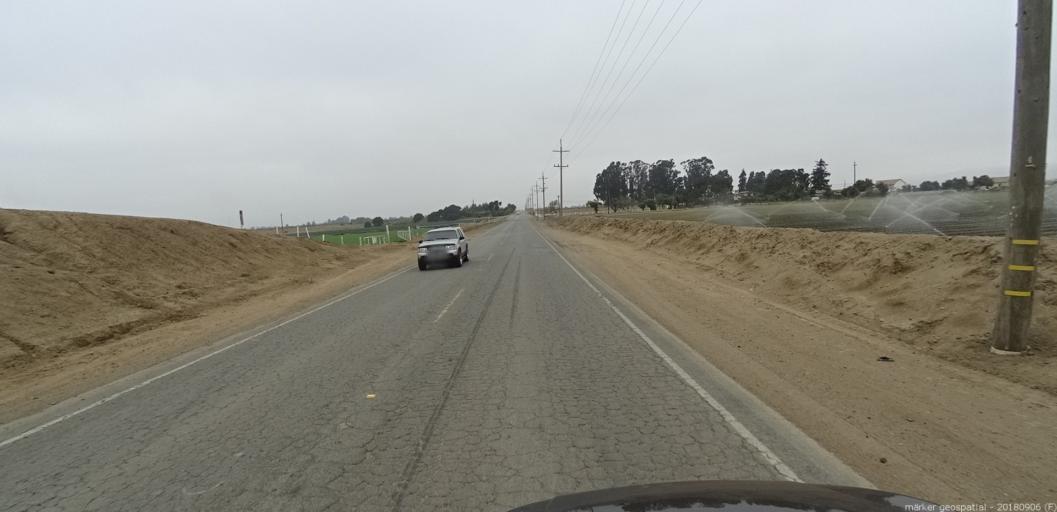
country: US
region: California
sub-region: Monterey County
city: Salinas
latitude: 36.6595
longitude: -121.5893
